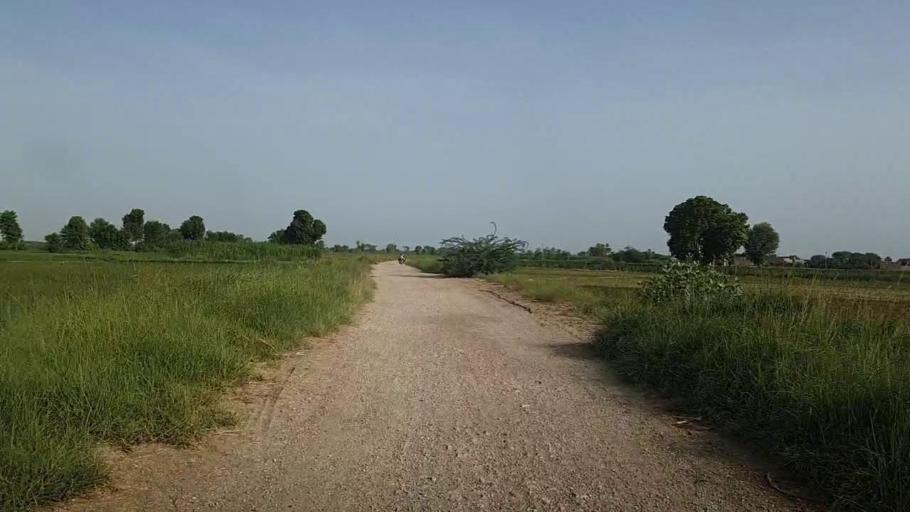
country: PK
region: Sindh
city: Pad Idan
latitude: 26.7535
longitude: 68.2567
